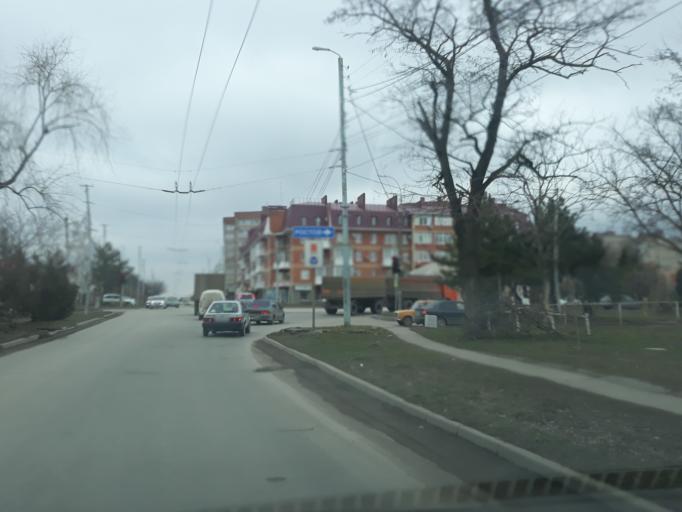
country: RU
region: Rostov
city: Taganrog
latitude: 47.2739
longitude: 38.9284
